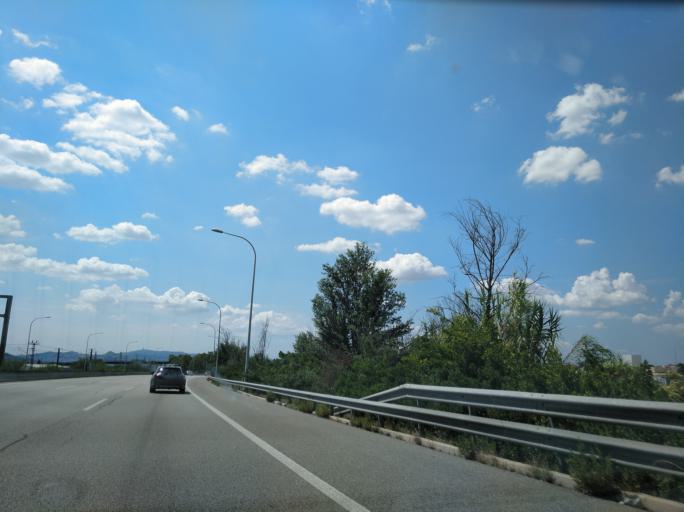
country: ES
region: Catalonia
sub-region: Provincia de Barcelona
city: Montmelo
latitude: 41.5457
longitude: 2.2335
